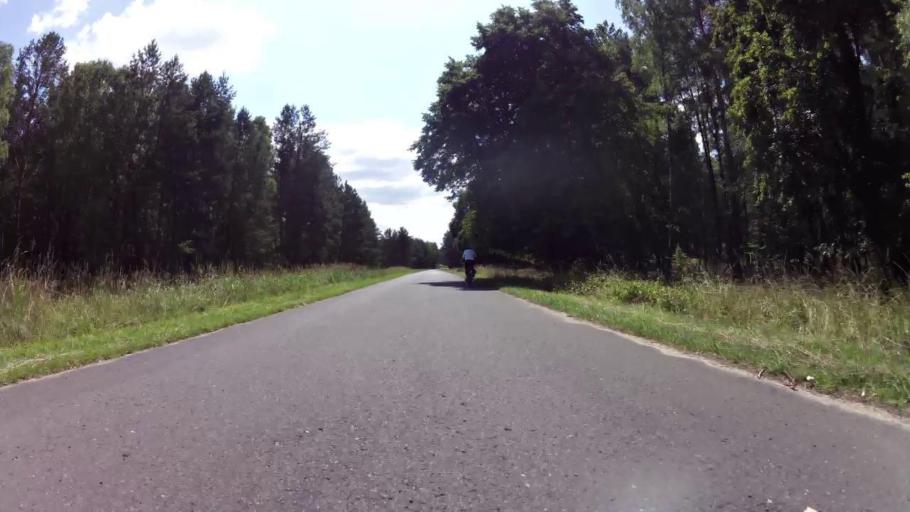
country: PL
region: West Pomeranian Voivodeship
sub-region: Powiat choszczenski
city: Drawno
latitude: 53.3812
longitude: 15.7290
